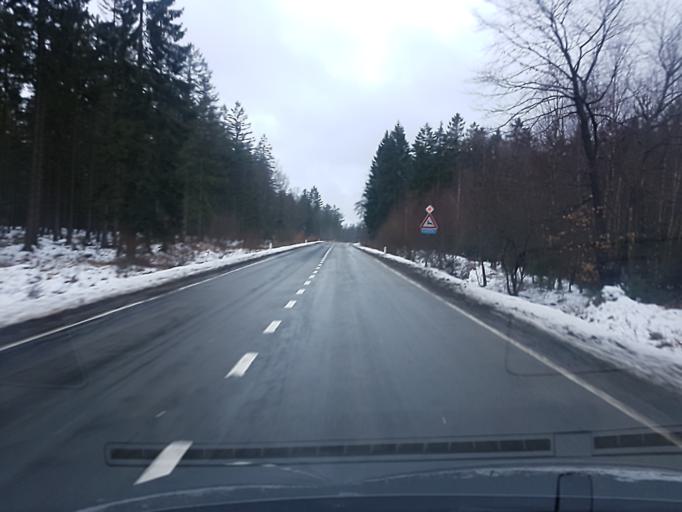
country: BE
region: Wallonia
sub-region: Province de Liege
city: Eupen
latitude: 50.5780
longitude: 6.0351
